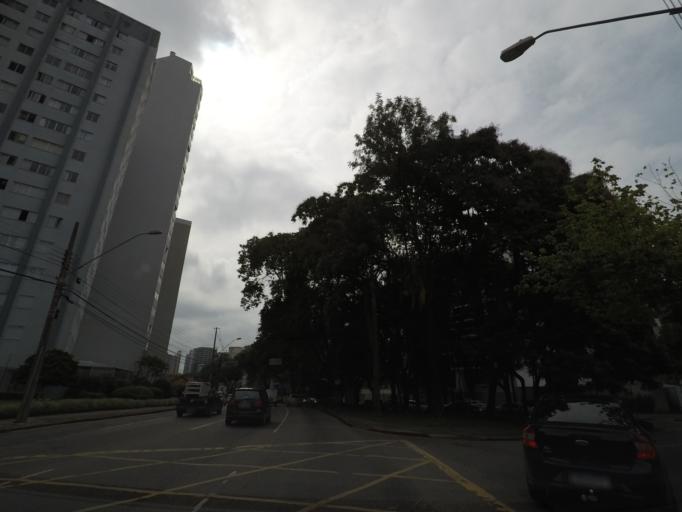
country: BR
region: Parana
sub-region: Curitiba
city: Curitiba
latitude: -25.4530
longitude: -49.2845
